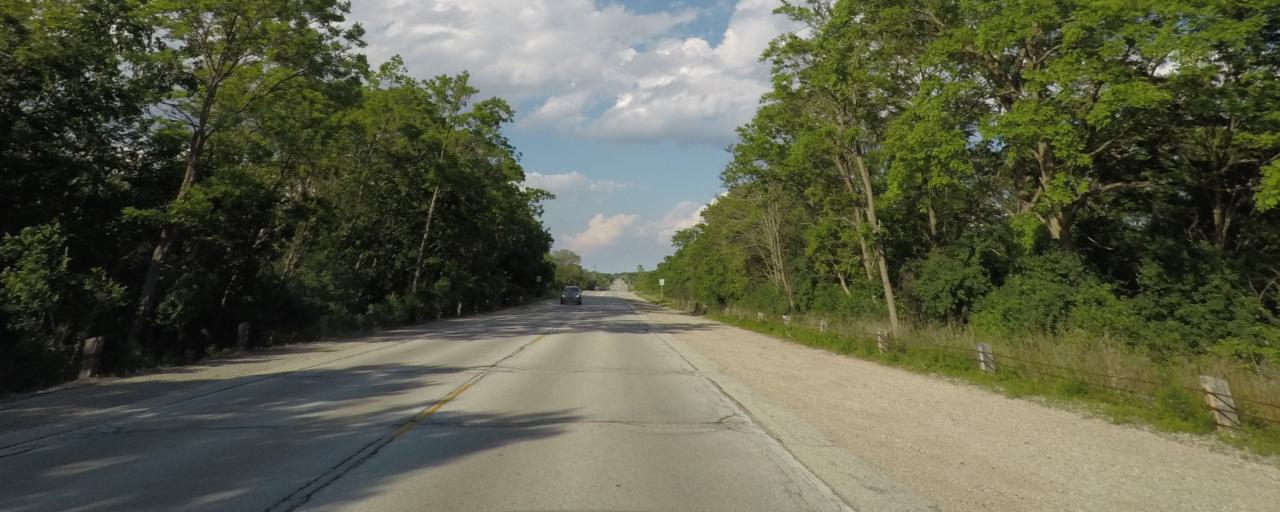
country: US
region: Wisconsin
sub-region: Milwaukee County
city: Hales Corners
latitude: 42.9689
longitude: -88.0599
